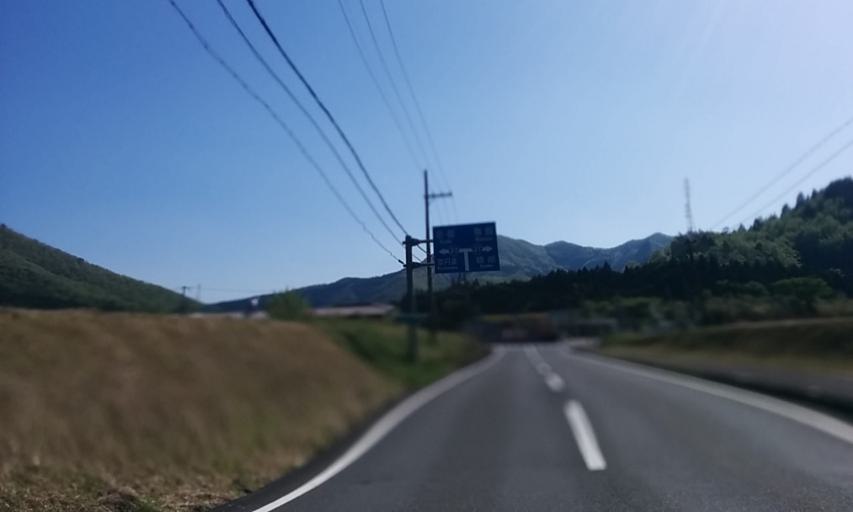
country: JP
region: Kyoto
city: Ayabe
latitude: 35.2496
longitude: 135.4194
